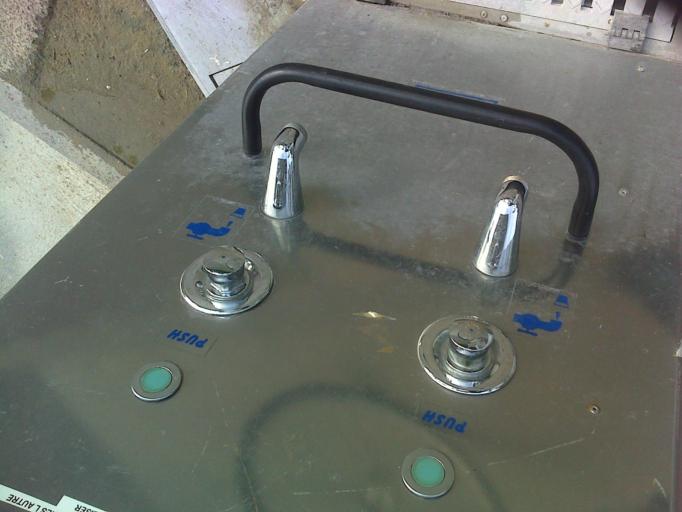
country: FR
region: Poitou-Charentes
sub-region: Departement de la Charente-Maritime
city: Les Mathes
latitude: 45.6914
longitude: -1.1892
